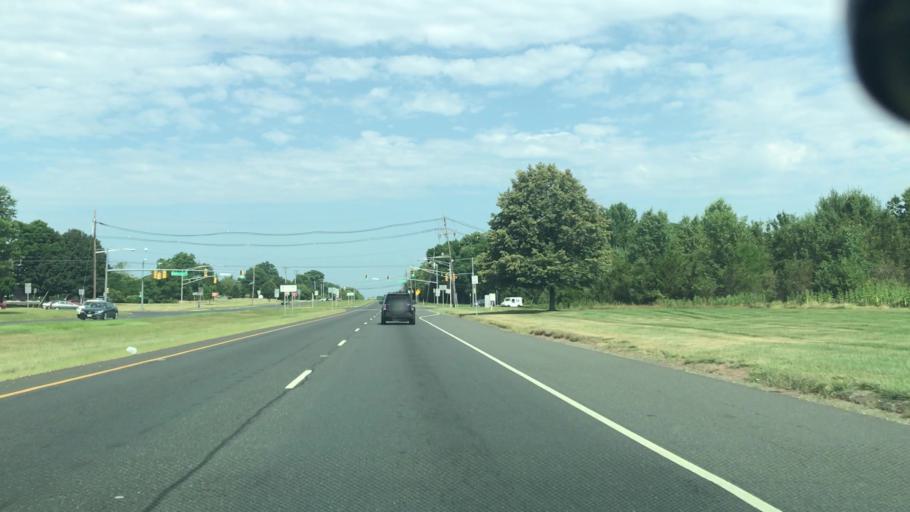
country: US
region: New Jersey
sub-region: Somerset County
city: Bridgewater
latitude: 40.5881
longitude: -74.6389
